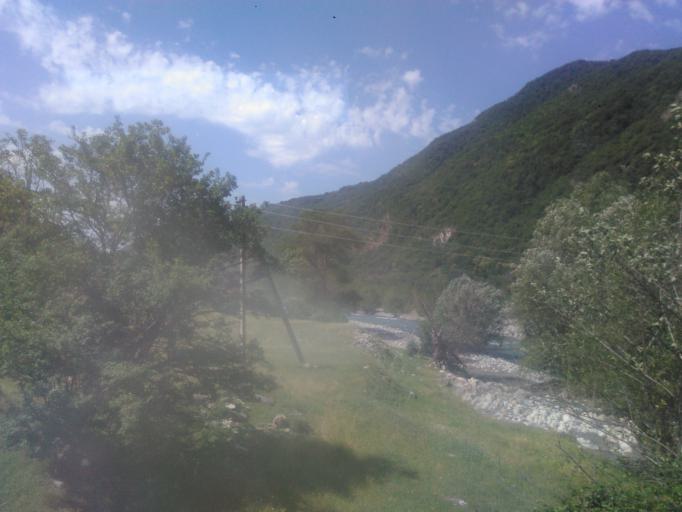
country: GE
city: Zhinvali
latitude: 42.2199
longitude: 44.8335
